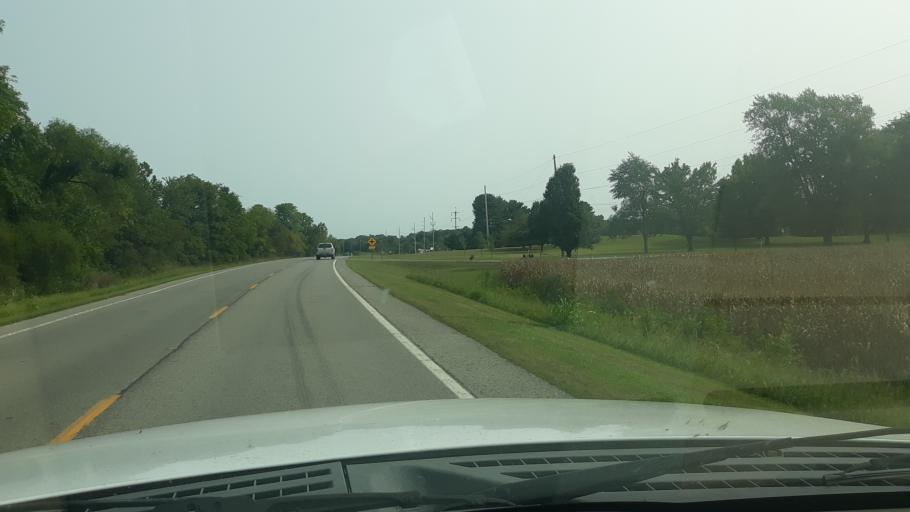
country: US
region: Illinois
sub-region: White County
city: Norris City
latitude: 37.9783
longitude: -88.3170
